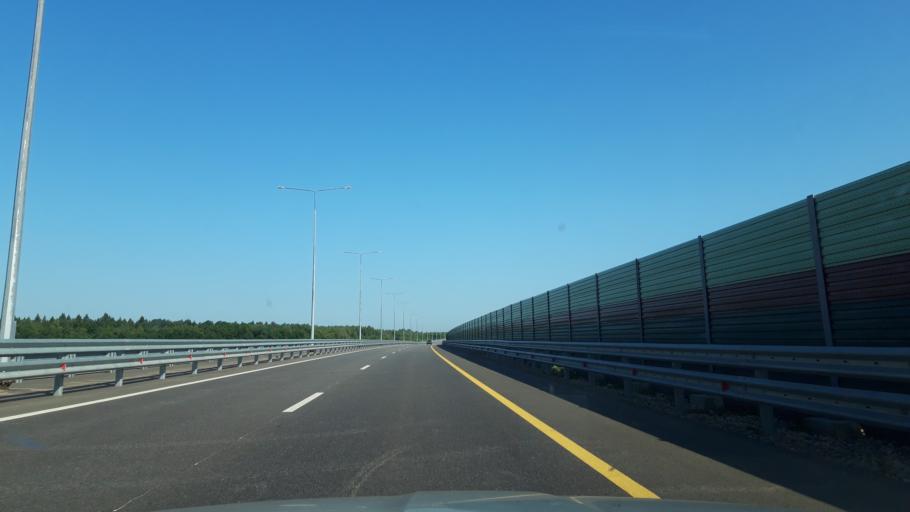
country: RU
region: Tverskaya
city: Zavidovo
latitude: 56.5124
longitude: 36.5097
